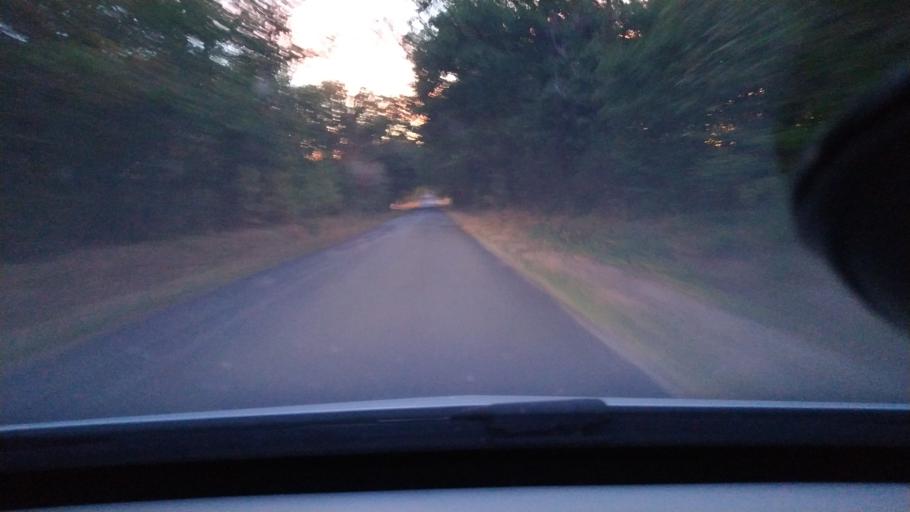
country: FR
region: Centre
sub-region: Departement du Cher
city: Brinon-sur-Sauldre
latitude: 47.6116
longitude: 2.1845
